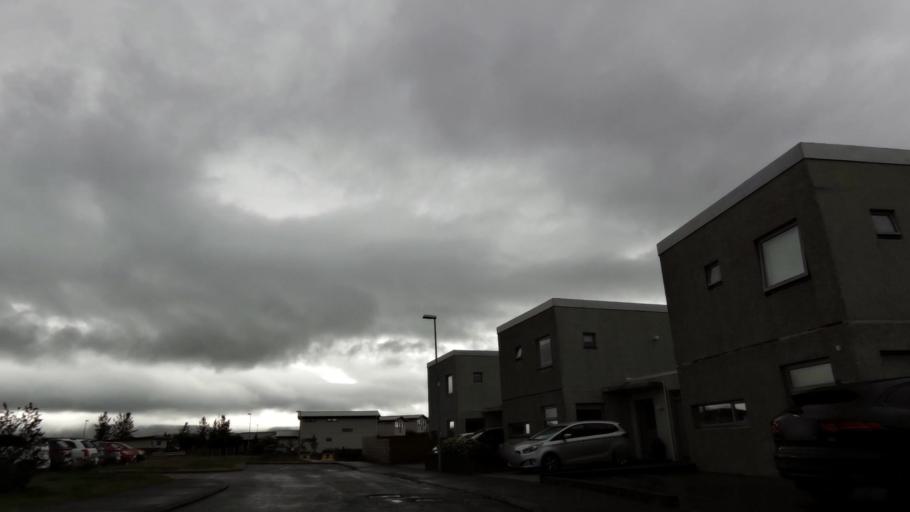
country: IS
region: Capital Region
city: Hafnarfjoerdur
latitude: 64.0486
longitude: -21.9766
